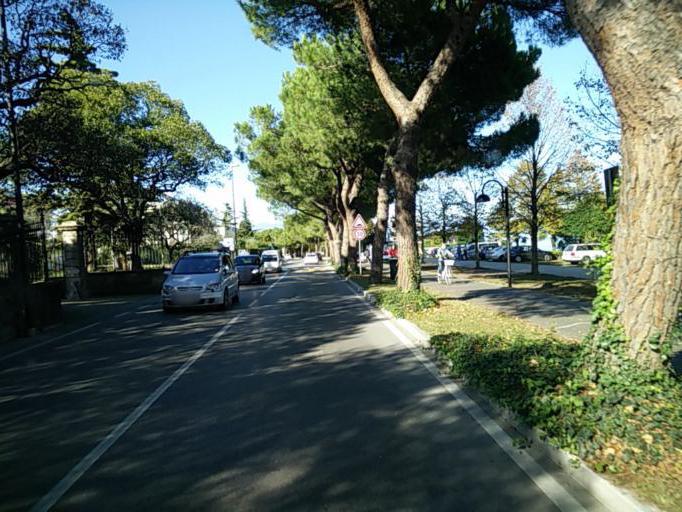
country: IT
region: Lombardy
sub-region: Provincia di Brescia
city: Sirmione
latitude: 45.4762
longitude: 10.6107
